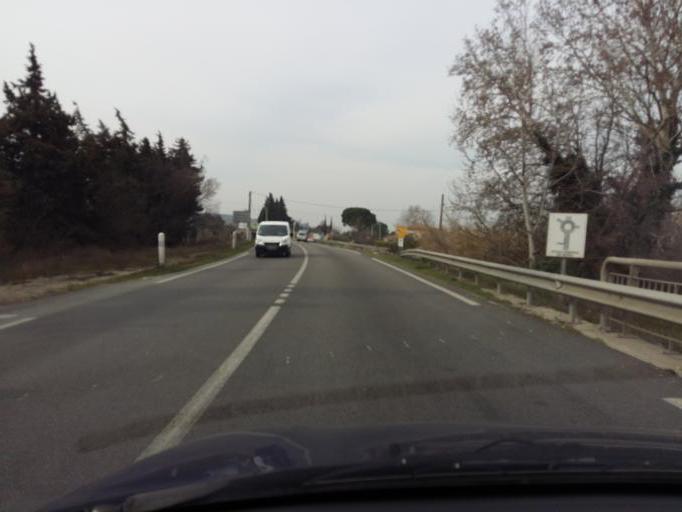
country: FR
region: Provence-Alpes-Cote d'Azur
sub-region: Departement des Bouches-du-Rhone
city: Noves
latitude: 43.8877
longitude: 4.8828
